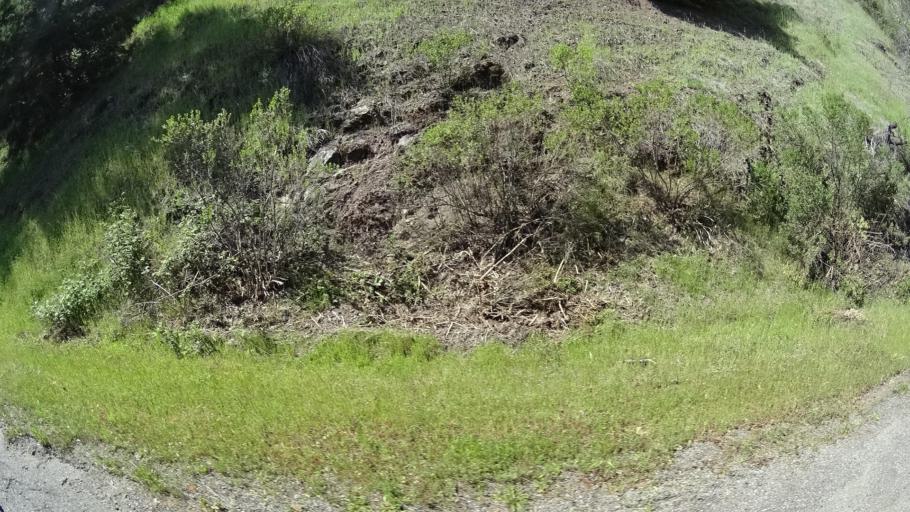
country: US
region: California
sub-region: Humboldt County
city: Redway
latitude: 40.2732
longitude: -123.6264
